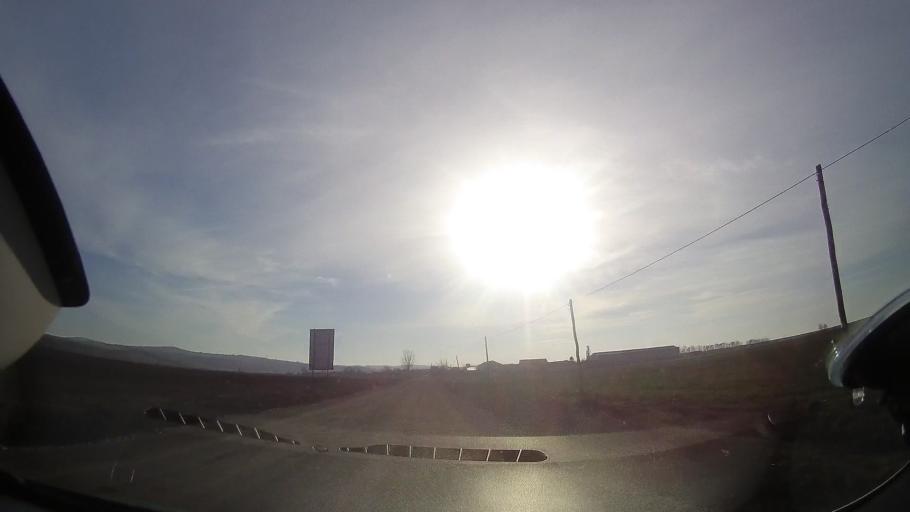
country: RO
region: Bihor
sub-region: Comuna Sarbi
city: Sarbi
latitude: 47.2149
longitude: 22.1332
